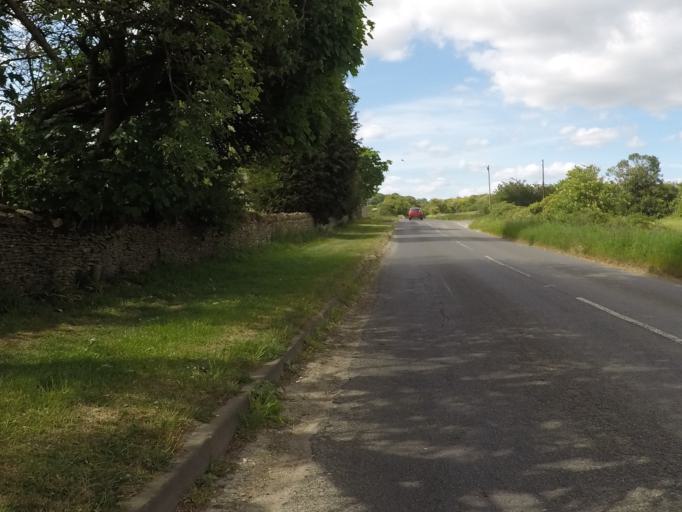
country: GB
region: England
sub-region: Oxfordshire
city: Witney
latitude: 51.8276
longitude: -1.5025
